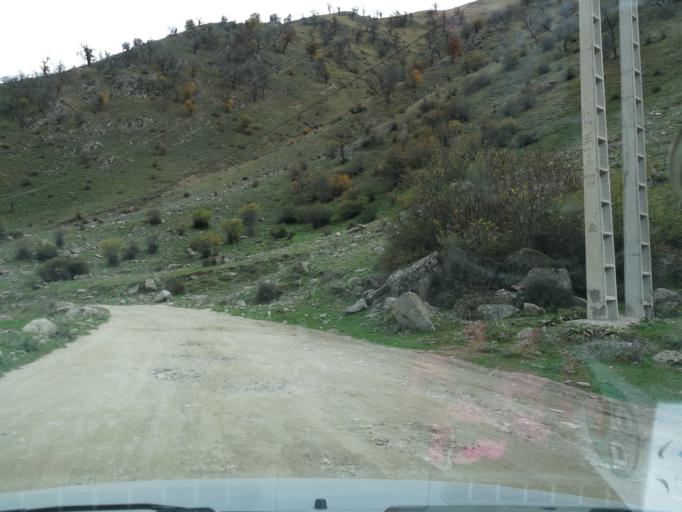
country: IR
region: Mazandaran
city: `Abbasabad
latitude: 36.4354
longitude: 51.0578
